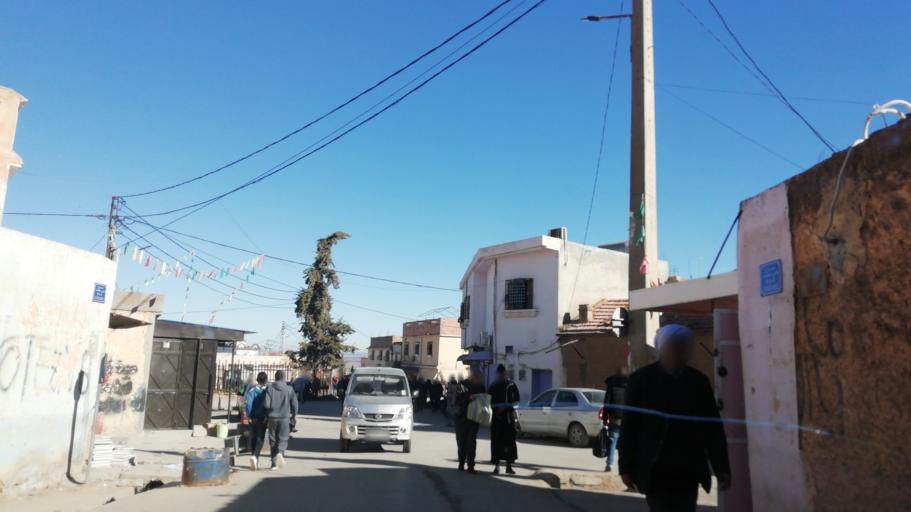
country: DZ
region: Tlemcen
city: Ouled Mimoun
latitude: 34.9015
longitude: -1.0393
